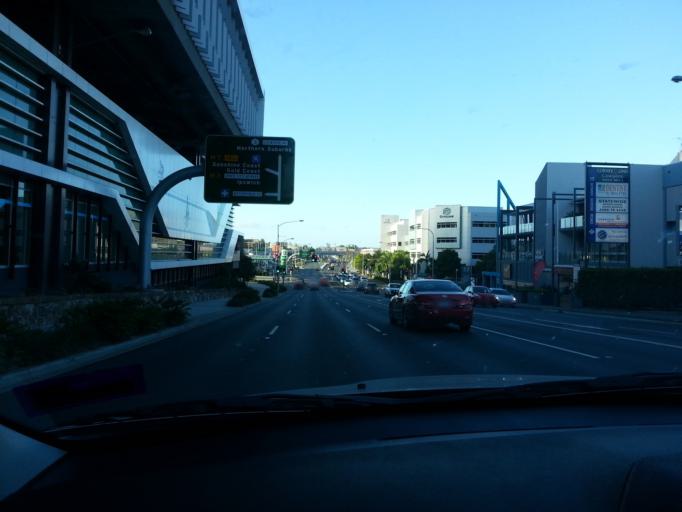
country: AU
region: Queensland
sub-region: Brisbane
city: Fortitude Valley
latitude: -27.4474
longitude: 153.0293
